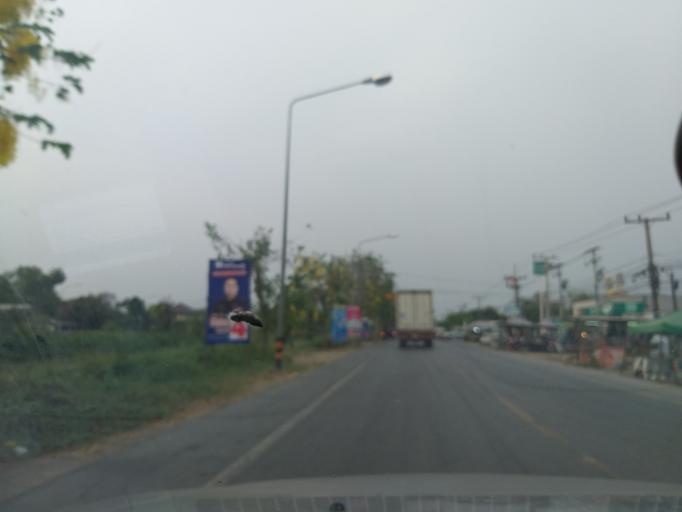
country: TH
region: Pathum Thani
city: Ban Lam Luk Ka
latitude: 14.0139
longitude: 100.8945
